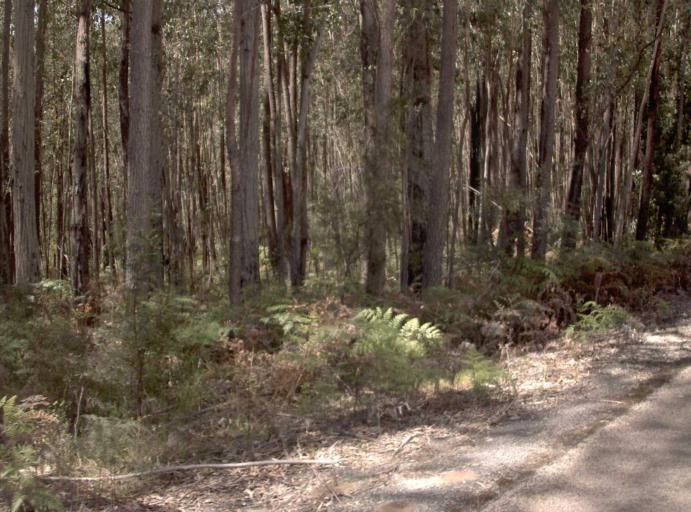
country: AU
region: New South Wales
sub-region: Bombala
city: Bombala
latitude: -37.5763
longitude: 149.3101
